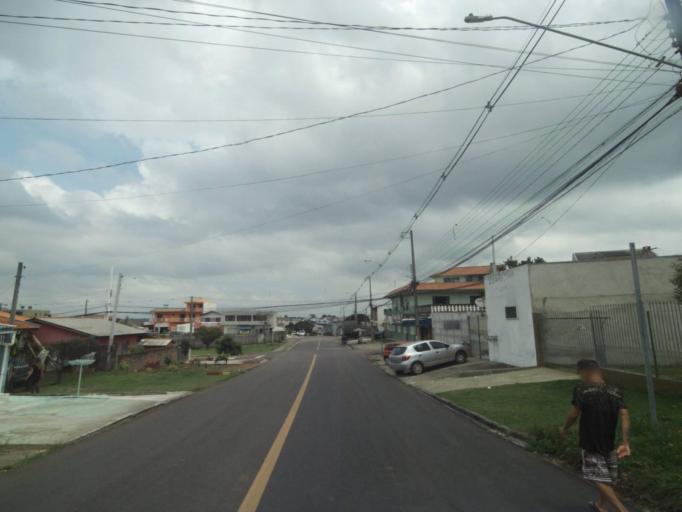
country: BR
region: Parana
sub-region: Curitiba
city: Curitiba
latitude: -25.4961
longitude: -49.3516
